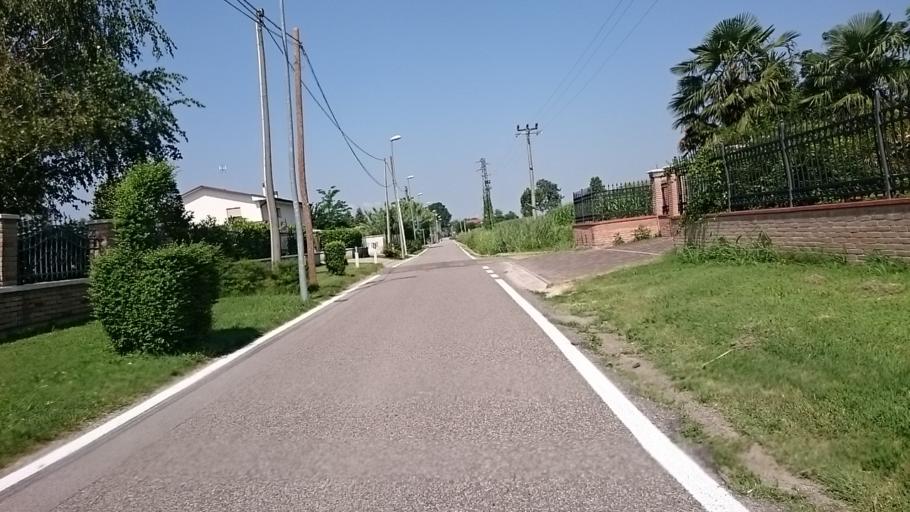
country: IT
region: Veneto
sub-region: Provincia di Padova
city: Albignasego
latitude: 45.3491
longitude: 11.9020
